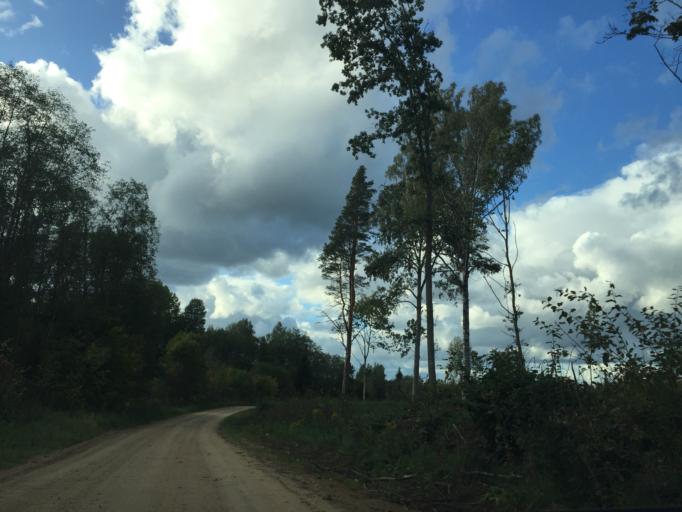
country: LV
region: Ligatne
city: Ligatne
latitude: 57.1315
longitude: 25.1040
